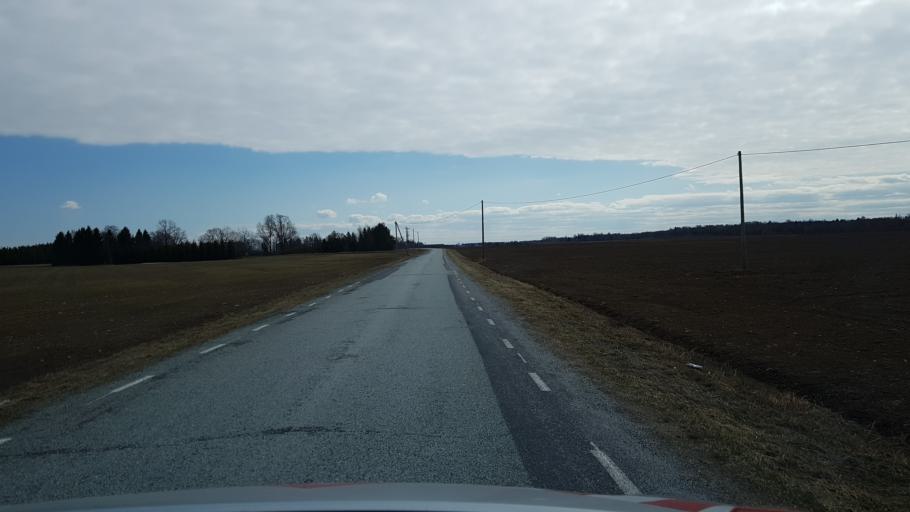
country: EE
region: Laeaene-Virumaa
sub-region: Haljala vald
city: Haljala
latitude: 59.4285
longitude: 26.2138
